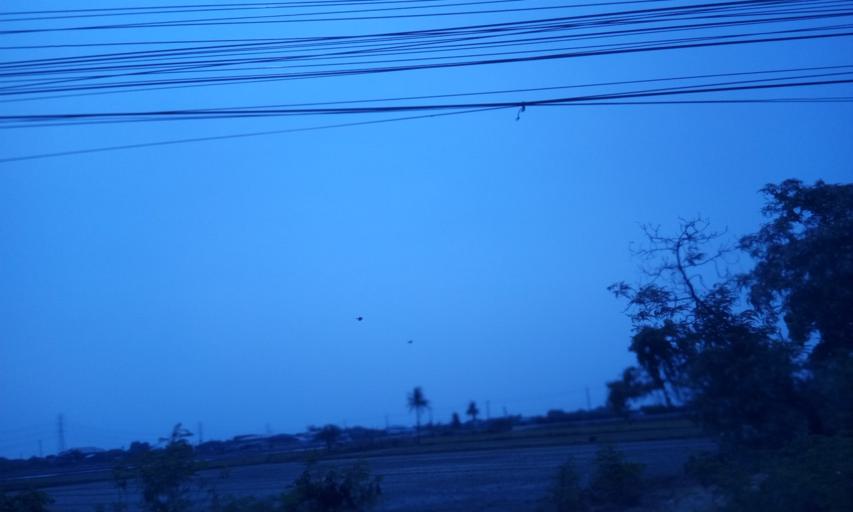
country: TH
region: Nonthaburi
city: Sai Noi
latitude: 13.9683
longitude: 100.3104
